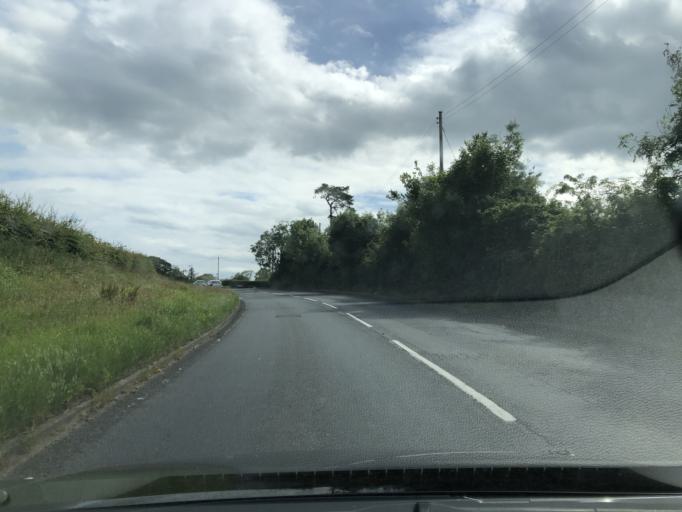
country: GB
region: Northern Ireland
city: Ballynahinch
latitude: 54.3899
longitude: -5.8833
